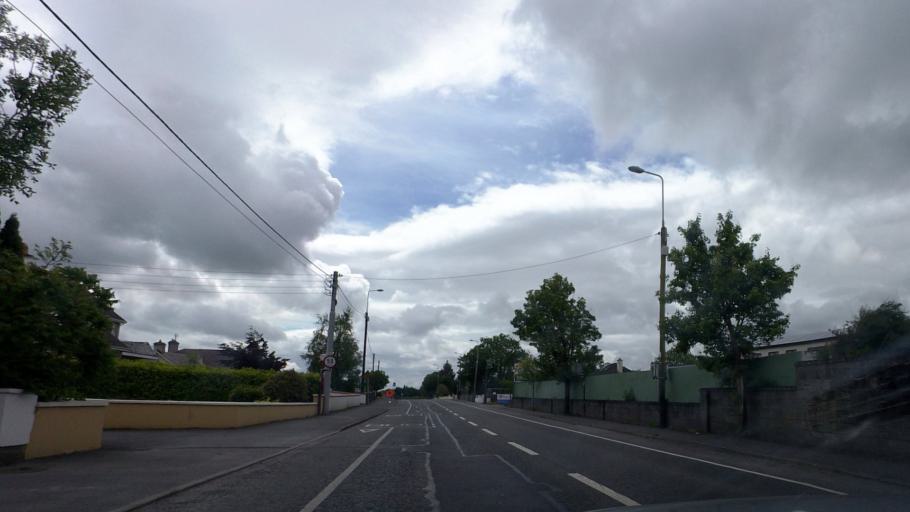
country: IE
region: Munster
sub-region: An Clar
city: Ennis
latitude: 52.8272
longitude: -8.9786
